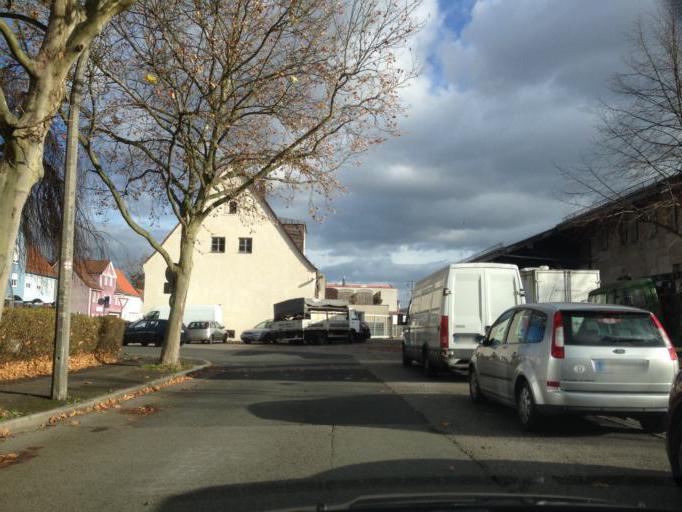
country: DE
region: Bavaria
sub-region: Regierungsbezirk Mittelfranken
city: Lauf an der Pegnitz
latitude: 49.5075
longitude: 11.2861
